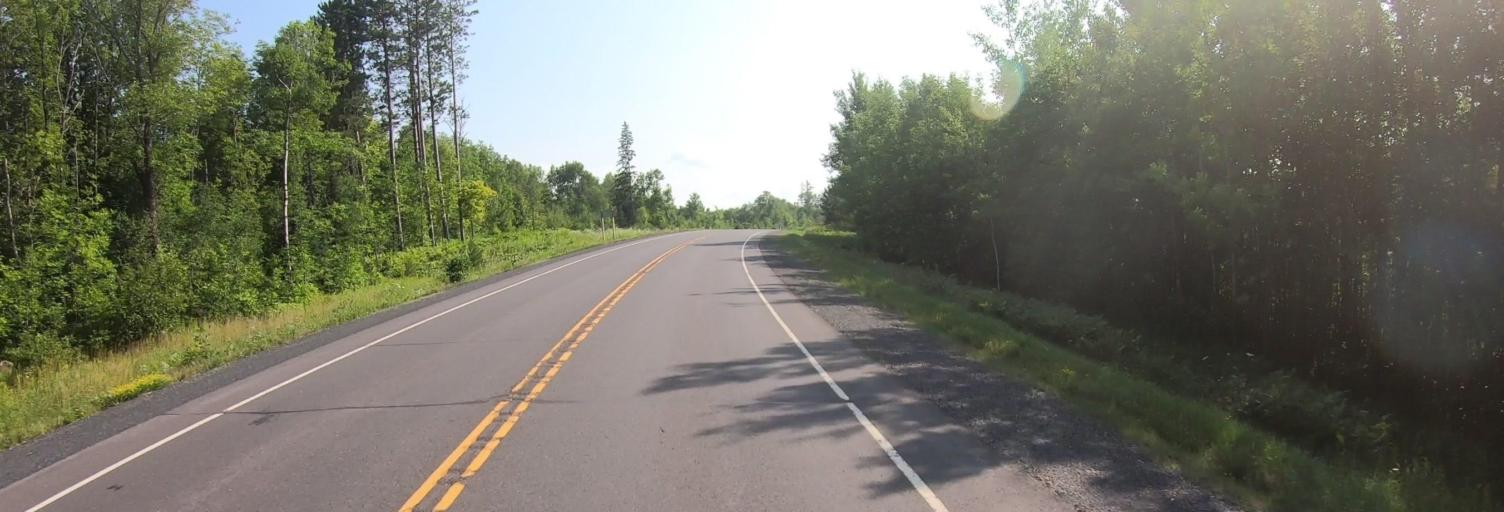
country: US
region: Wisconsin
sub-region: Iron County
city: Hurley
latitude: 46.4234
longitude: -90.2600
